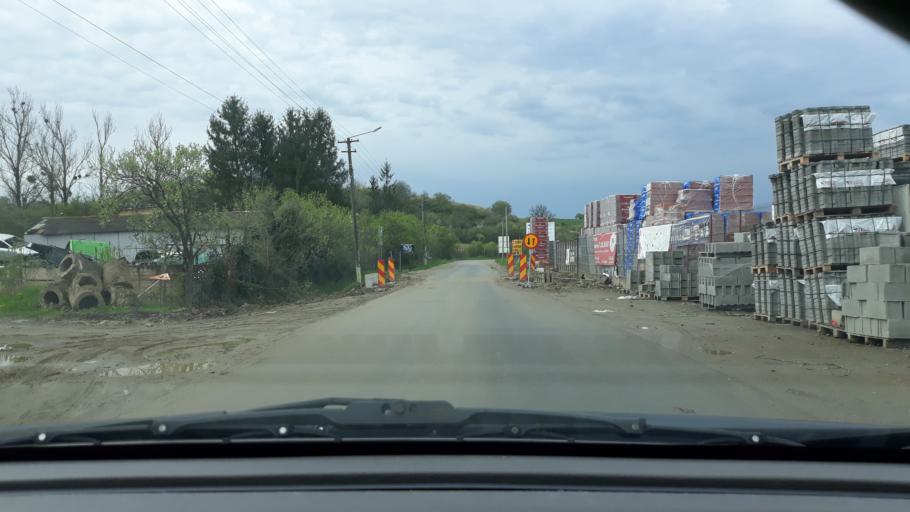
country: RO
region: Salaj
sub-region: Comuna Cehu Silvaniei
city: Cehu Silvaniei
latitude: 47.4041
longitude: 23.1615
